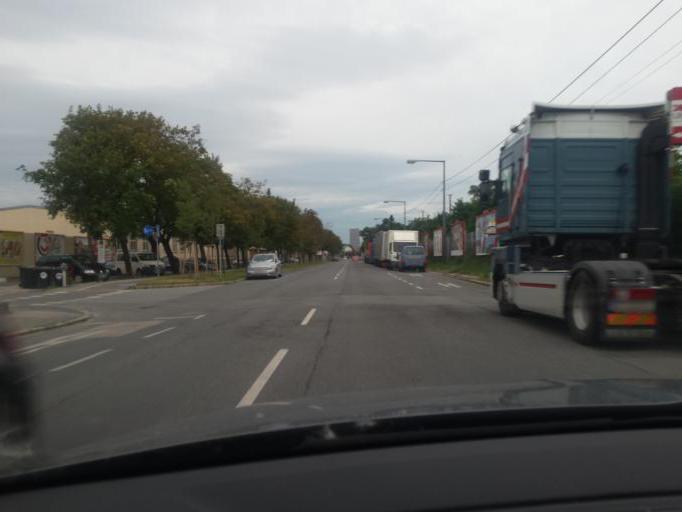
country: AT
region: Lower Austria
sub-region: Politischer Bezirk Wien-Umgebung
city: Schwechat
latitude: 48.1826
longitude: 16.4293
